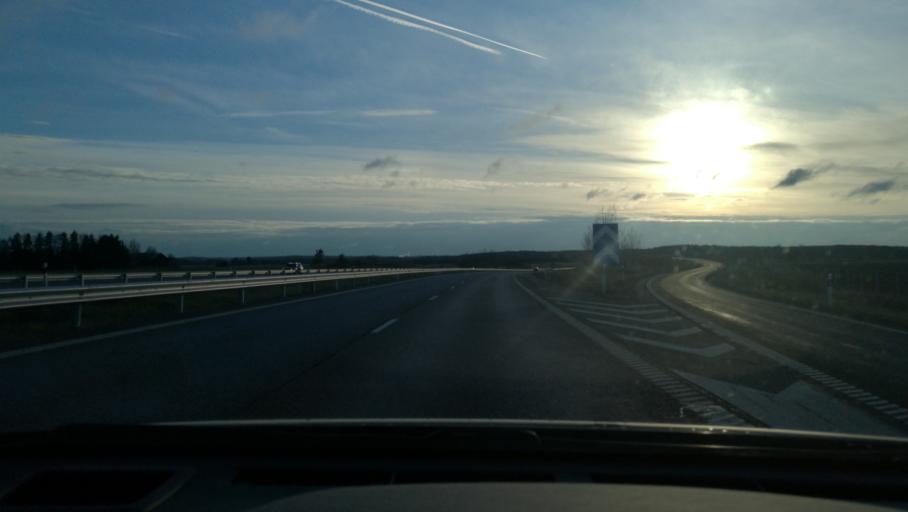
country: SE
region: Vaestmanland
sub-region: Arboga Kommun
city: Arboga
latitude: 59.4369
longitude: 15.8983
